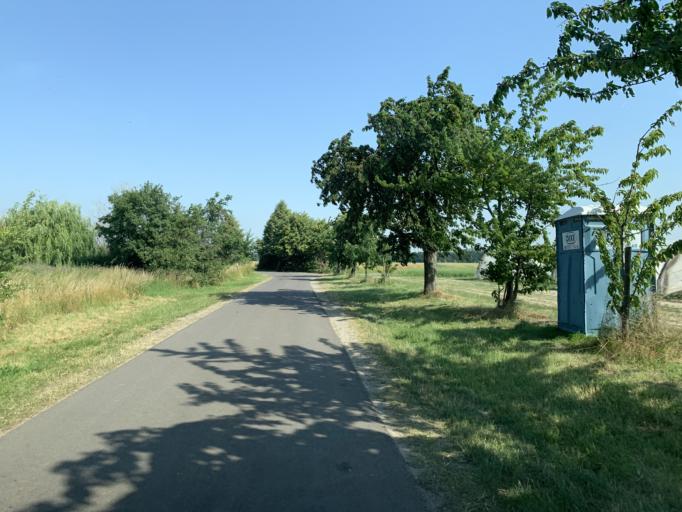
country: DE
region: Saxony-Anhalt
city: Erxleben
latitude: 52.2237
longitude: 11.2307
